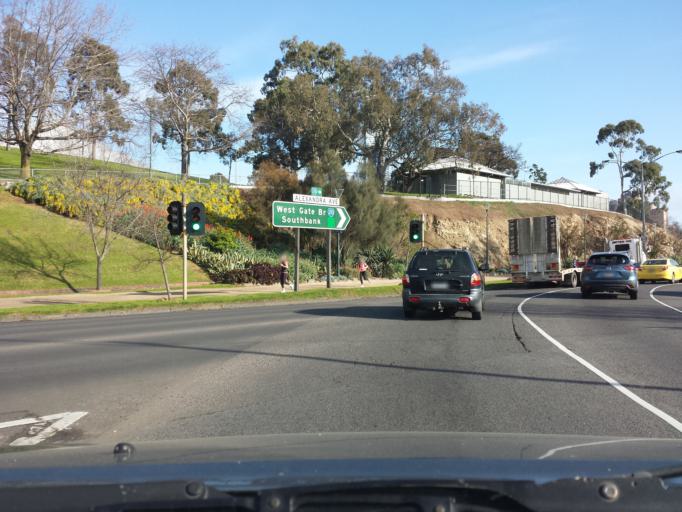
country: AU
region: Victoria
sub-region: Melbourne
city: Southbank
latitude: -37.8232
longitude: 144.9763
